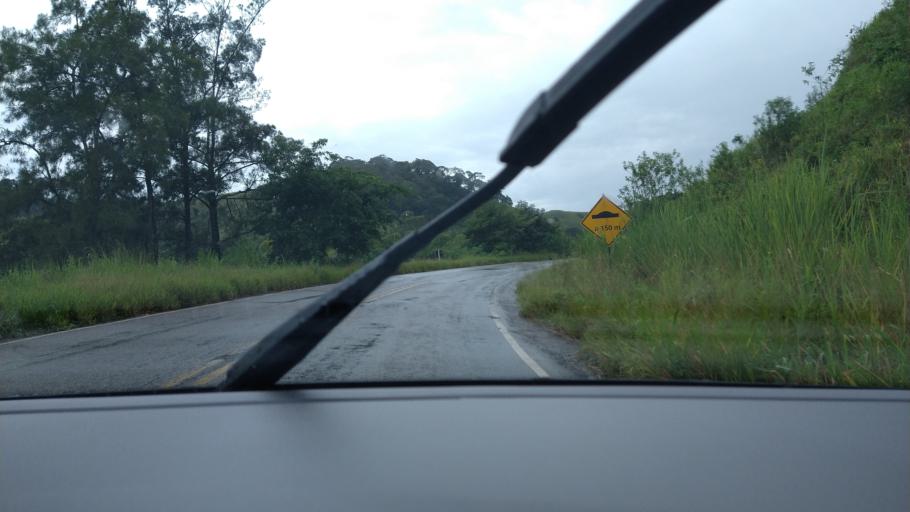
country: BR
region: Minas Gerais
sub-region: Ponte Nova
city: Ponte Nova
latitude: -20.3790
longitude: -42.9016
